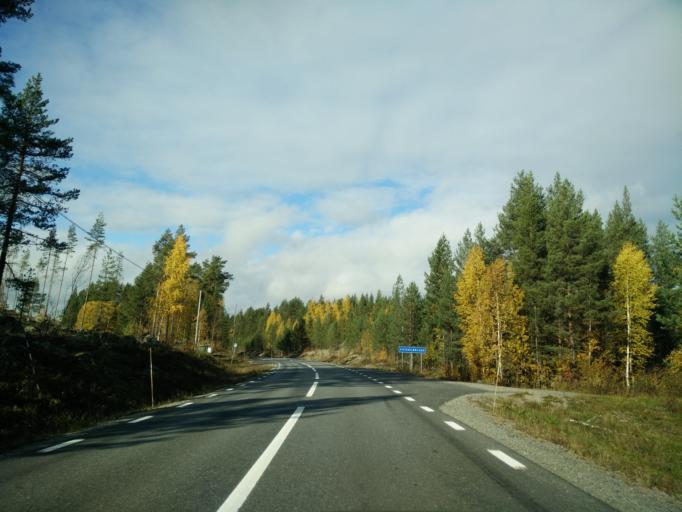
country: SE
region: Jaemtland
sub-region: Braecke Kommun
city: Braecke
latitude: 62.3893
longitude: 15.1043
